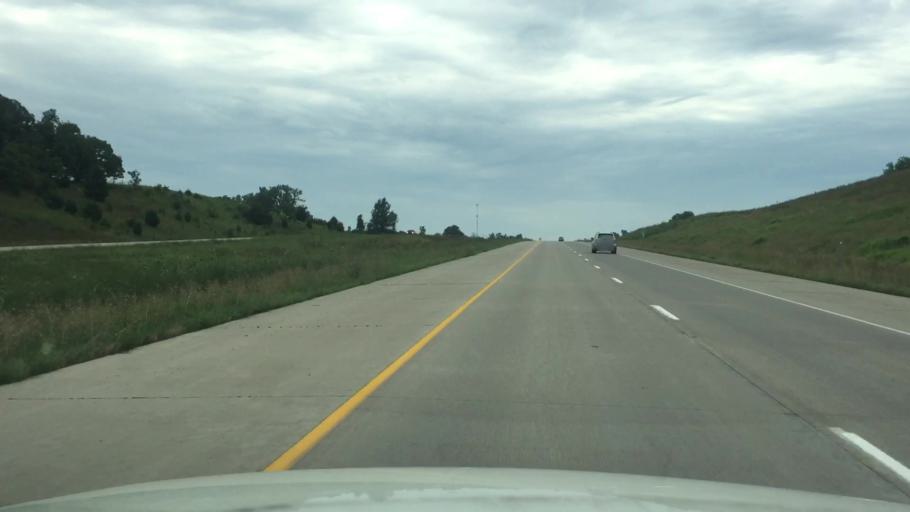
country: US
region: Iowa
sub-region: Warren County
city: Norwalk
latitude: 41.4539
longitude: -93.7801
